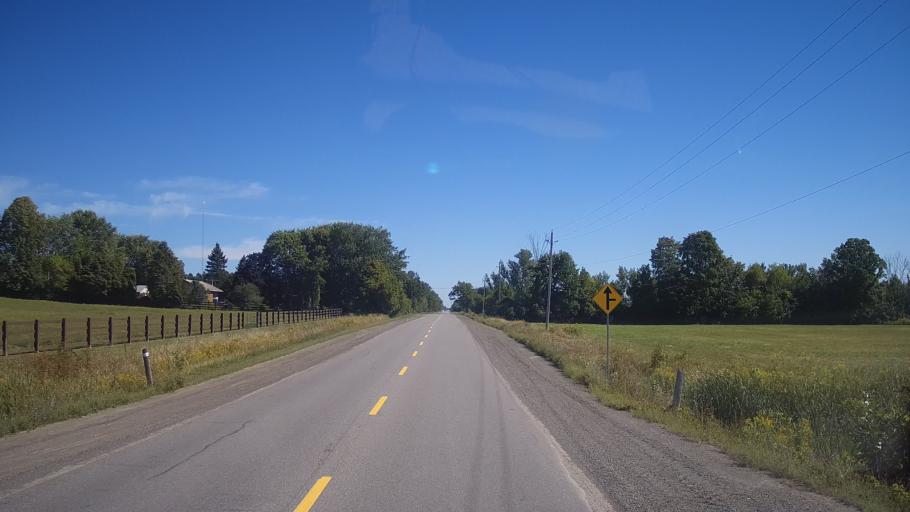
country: CA
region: Ontario
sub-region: Lanark County
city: Smiths Falls
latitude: 45.0080
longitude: -75.7579
